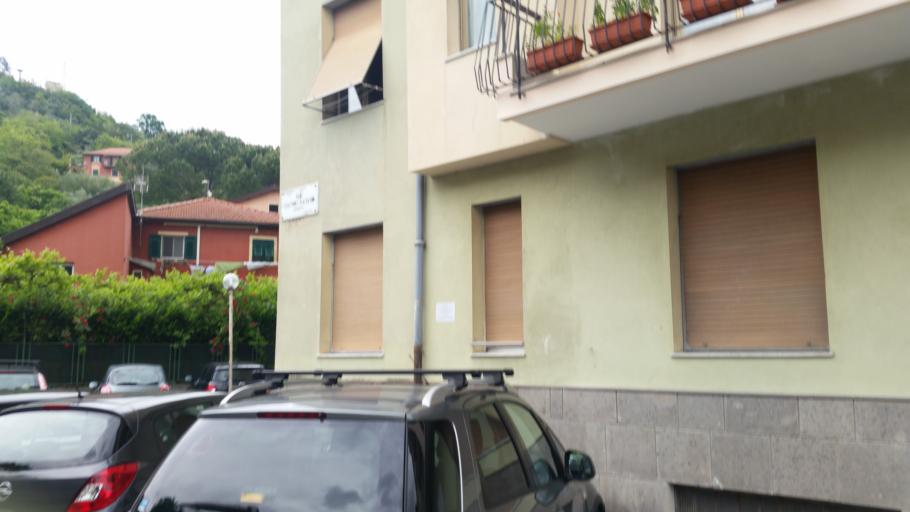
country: IT
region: Liguria
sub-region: Provincia di Genova
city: Piccarello
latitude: 44.4501
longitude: 9.0195
